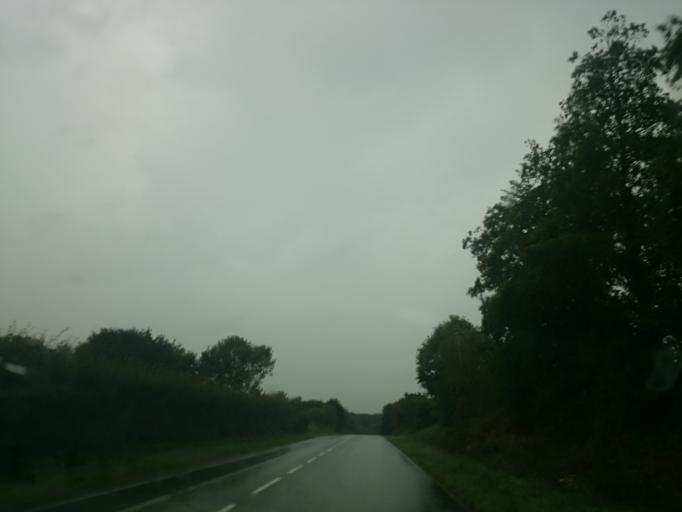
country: FR
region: Brittany
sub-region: Departement du Finistere
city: Plouvien
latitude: 48.5307
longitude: -4.4696
